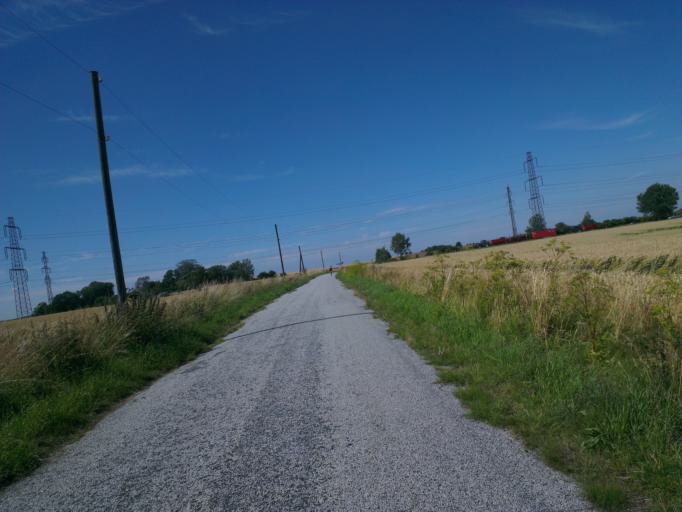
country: DK
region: Capital Region
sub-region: Frederikssund Kommune
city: Slangerup
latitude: 55.8533
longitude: 12.1629
